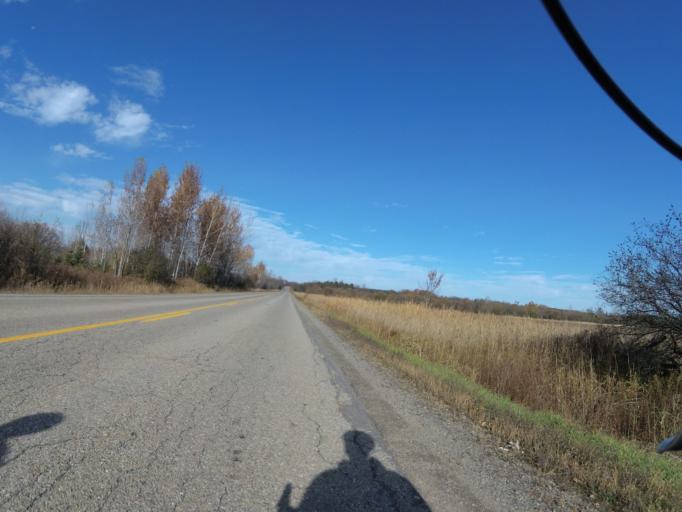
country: CA
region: Ontario
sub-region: Lanark County
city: Smiths Falls
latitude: 44.8297
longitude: -75.9379
